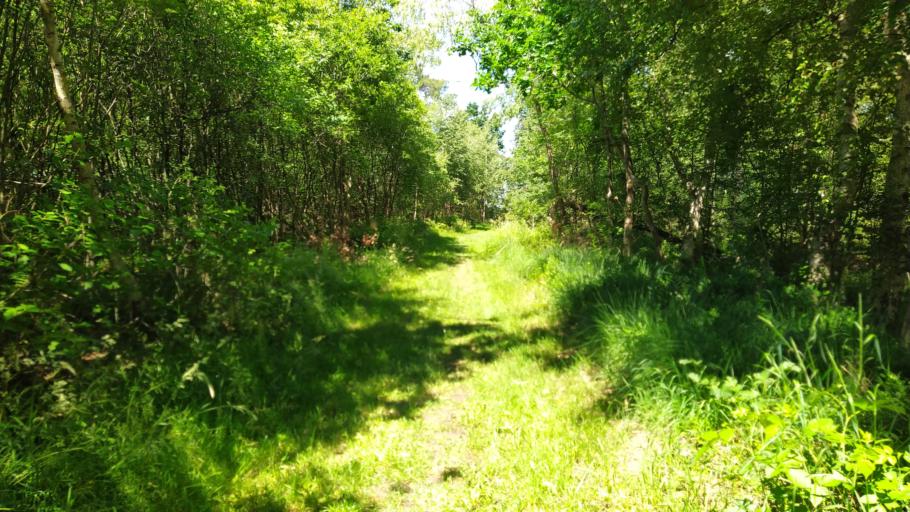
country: DE
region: Lower Saxony
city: Oldendorf
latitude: 53.5622
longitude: 9.2537
